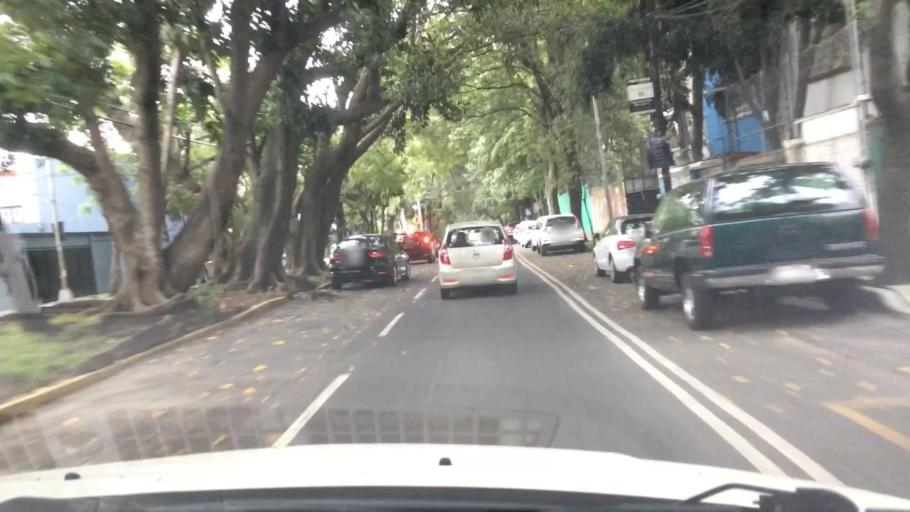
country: MX
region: Mexico City
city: Alvaro Obregon
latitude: 19.3548
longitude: -99.1884
